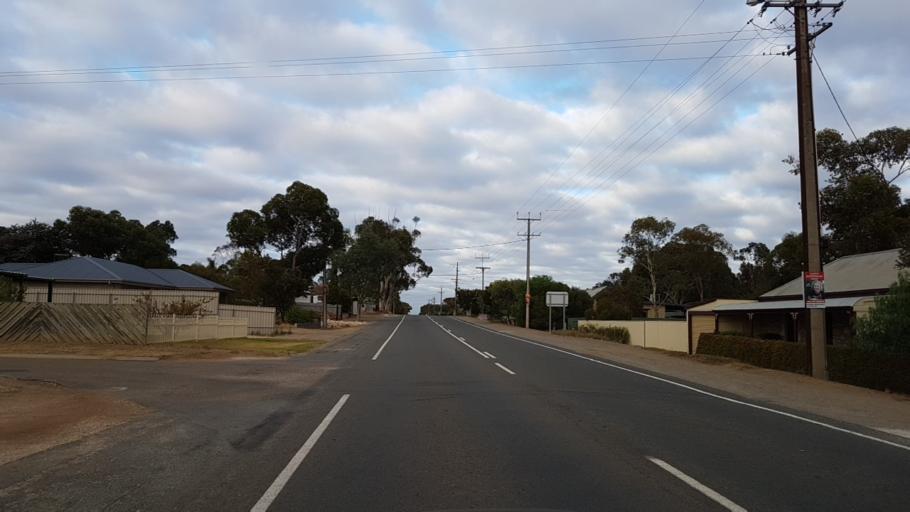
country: AU
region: South Australia
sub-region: Mount Barker
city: Callington
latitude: -35.1176
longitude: 139.0425
